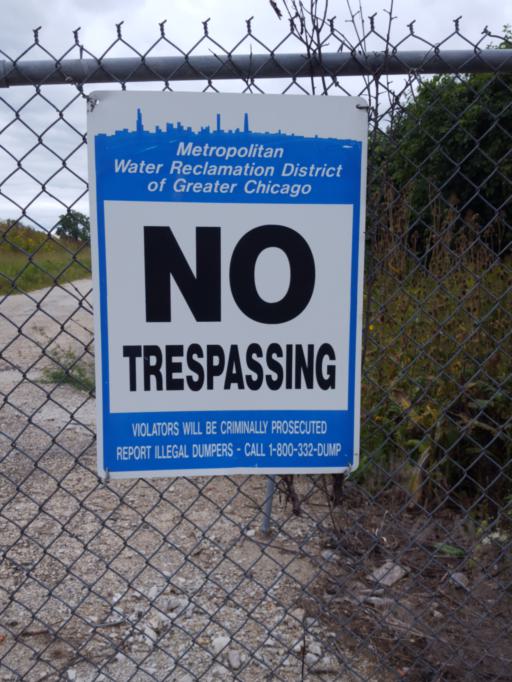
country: US
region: Illinois
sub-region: Lake County
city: Deerfield
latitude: 42.1527
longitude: -87.8526
